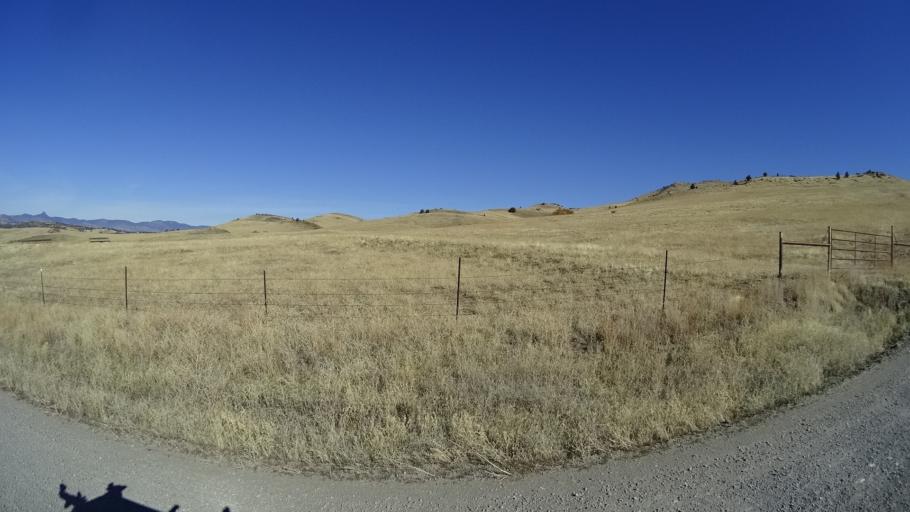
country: US
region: California
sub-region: Siskiyou County
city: Montague
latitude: 41.8455
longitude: -122.4323
